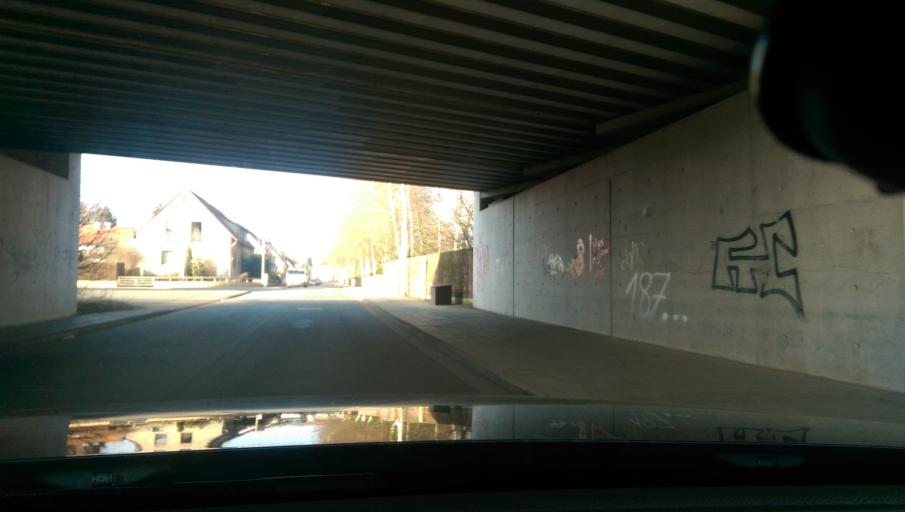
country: DE
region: Lower Saxony
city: Langenhagen
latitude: 52.4181
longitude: 9.7015
